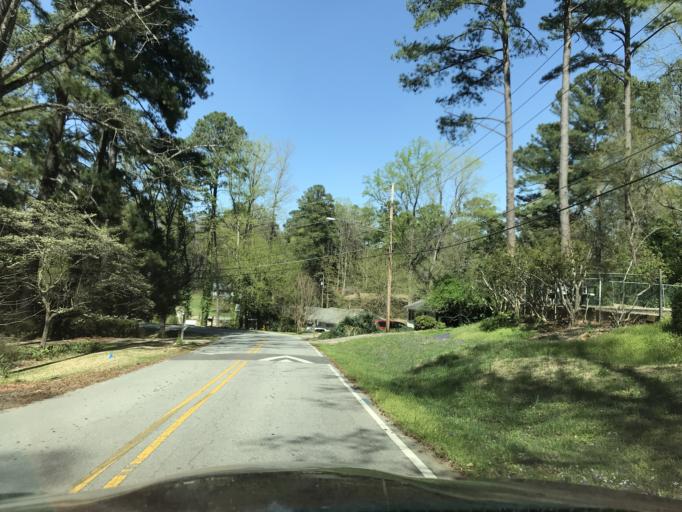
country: US
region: North Carolina
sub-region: Wake County
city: West Raleigh
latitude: 35.7699
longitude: -78.7075
